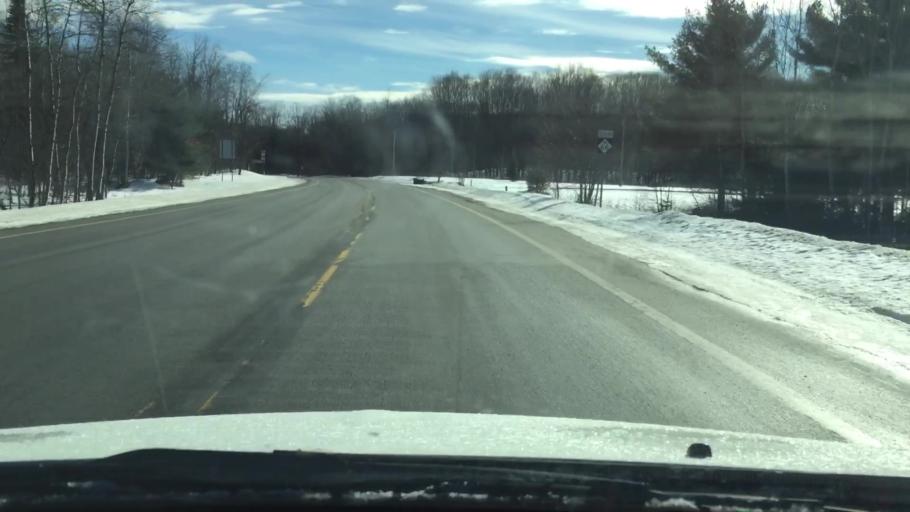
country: US
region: Michigan
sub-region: Antrim County
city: Mancelona
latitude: 44.9927
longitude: -85.0620
